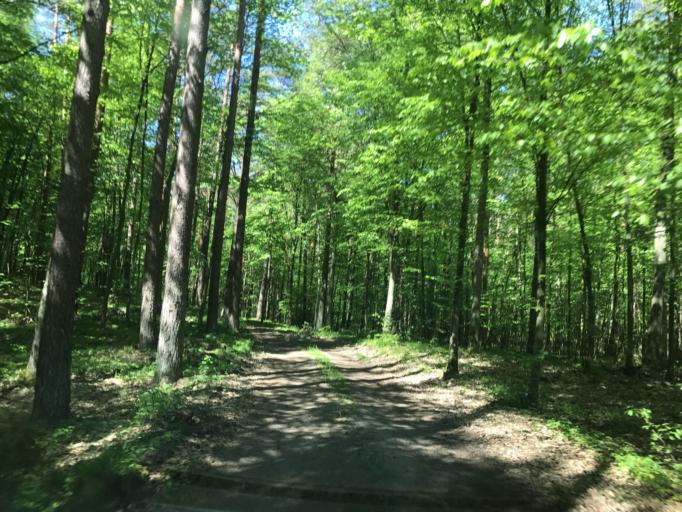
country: PL
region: Kujawsko-Pomorskie
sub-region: Powiat brodnicki
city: Gorzno
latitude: 53.2142
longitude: 19.7299
